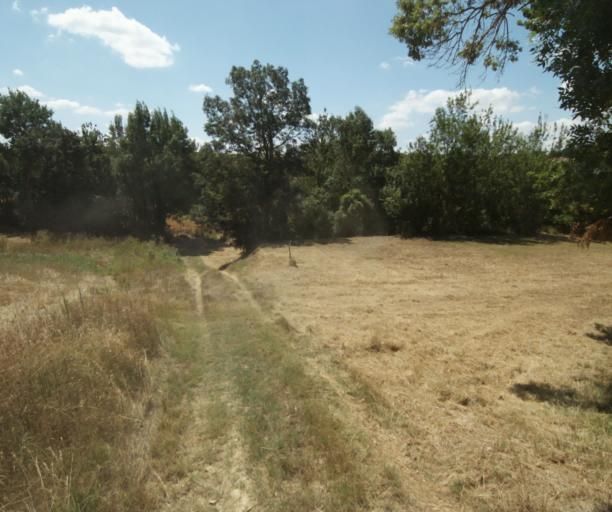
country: FR
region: Midi-Pyrenees
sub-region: Departement de la Haute-Garonne
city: Auriac-sur-Vendinelle
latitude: 43.4797
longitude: 1.8483
